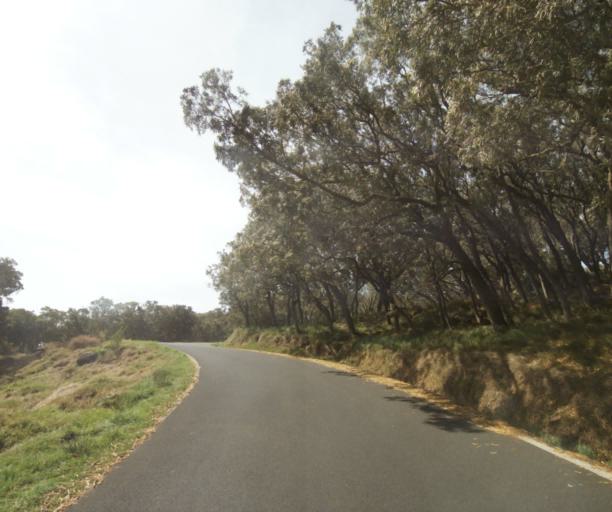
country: RE
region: Reunion
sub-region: Reunion
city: Trois-Bassins
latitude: -21.0615
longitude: 55.3761
